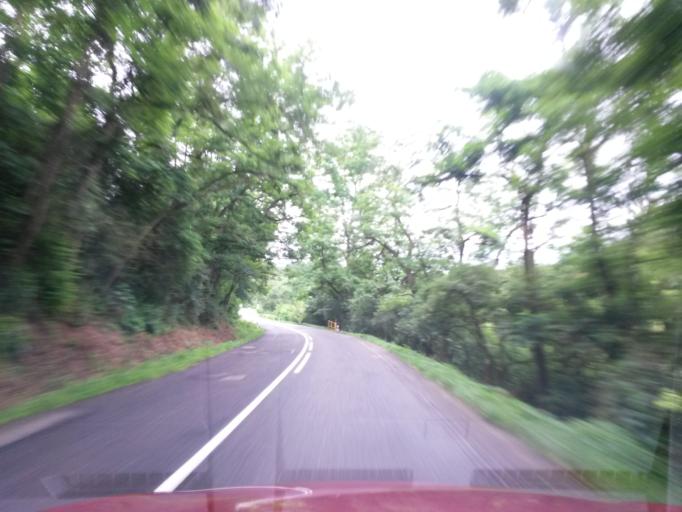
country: SK
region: Banskobystricky
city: Dudince
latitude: 48.1562
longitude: 18.9138
